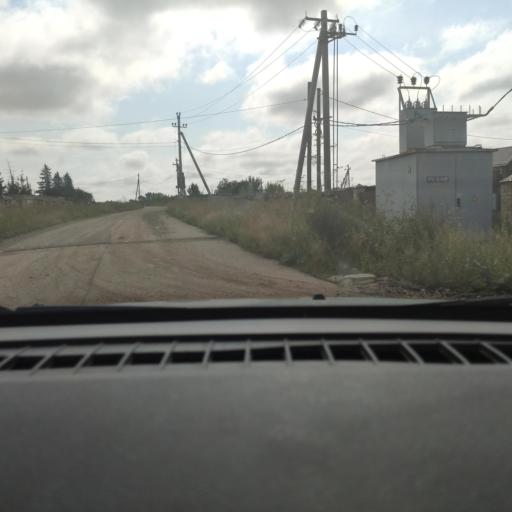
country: RU
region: Perm
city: Lobanovo
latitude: 57.8698
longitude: 56.2781
